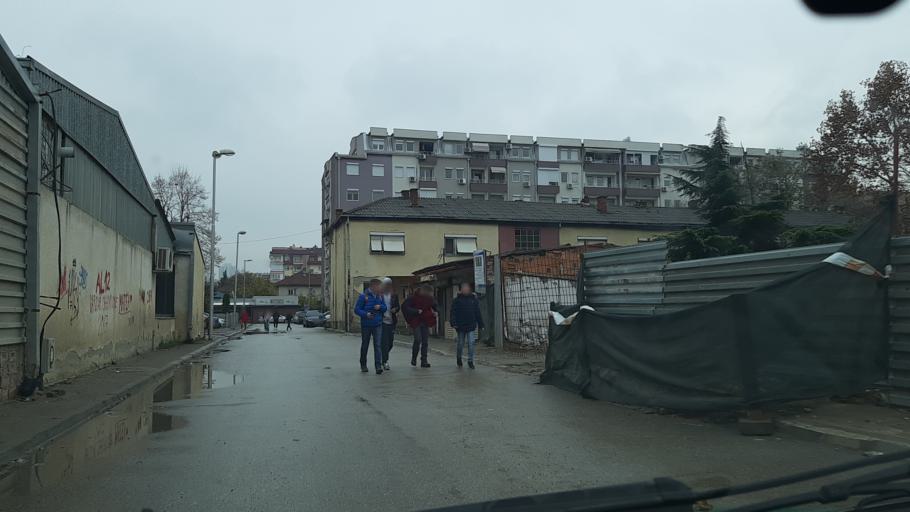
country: MK
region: Karpos
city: Skopje
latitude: 41.9883
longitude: 21.4449
